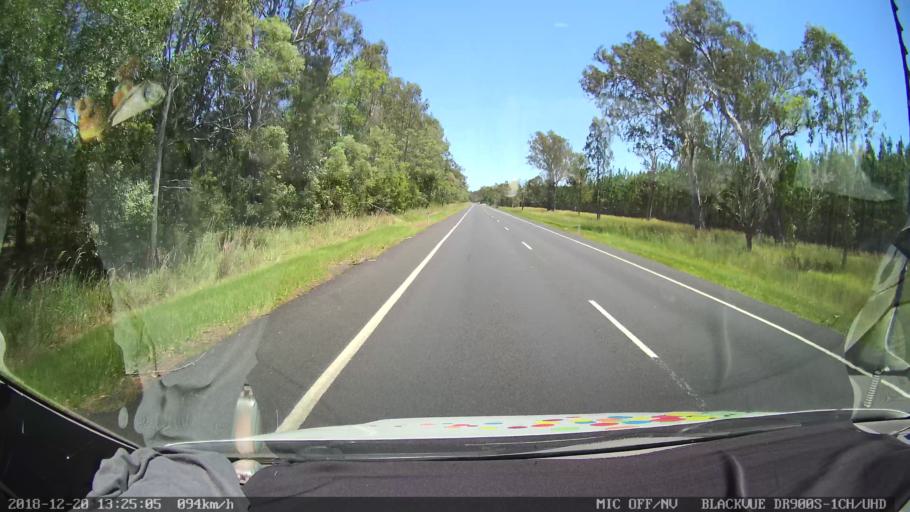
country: AU
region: New South Wales
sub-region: Richmond Valley
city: Casino
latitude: -29.1261
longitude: 152.9978
